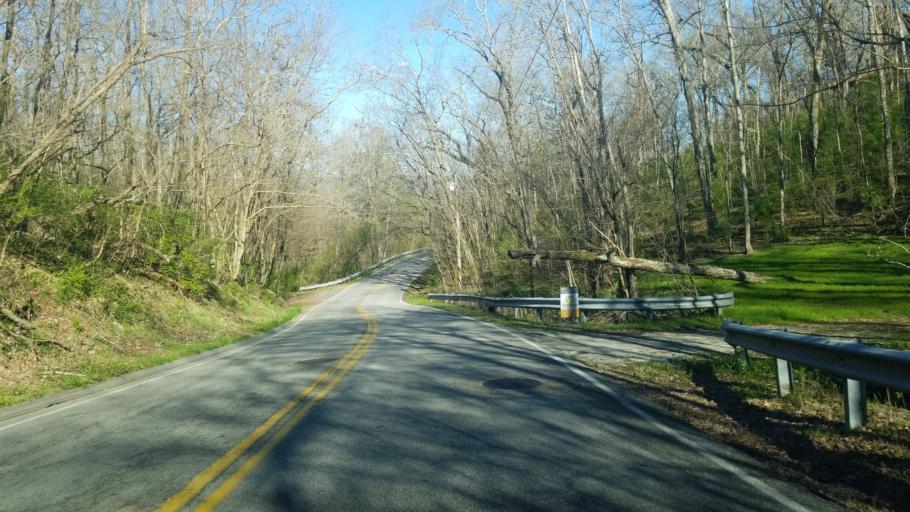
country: US
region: Tennessee
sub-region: Hamilton County
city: East Chattanooga
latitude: 35.1226
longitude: -85.2149
